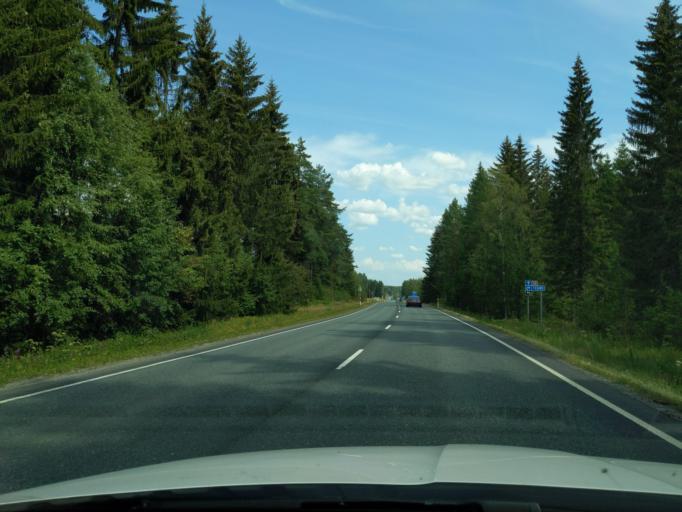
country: FI
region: Haeme
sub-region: Haemeenlinna
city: Tuulos
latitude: 61.1002
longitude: 24.8435
